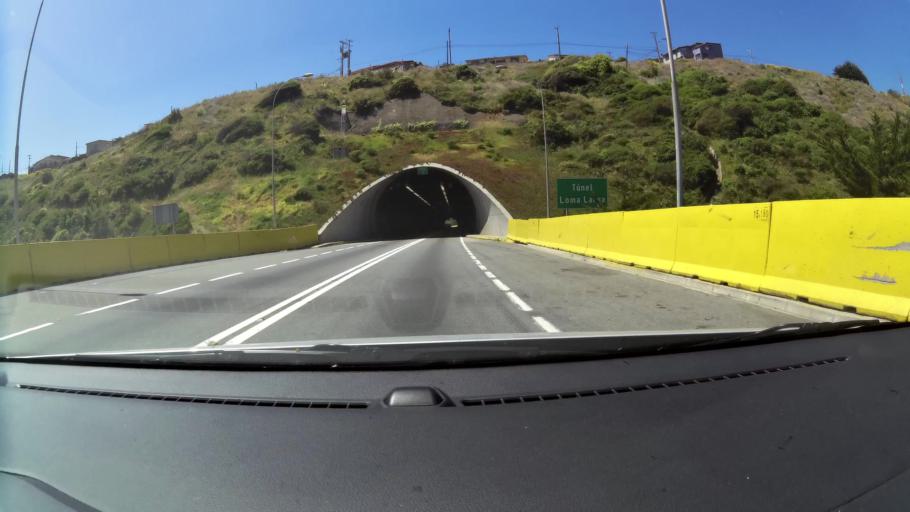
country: CL
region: Valparaiso
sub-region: Provincia de Valparaiso
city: Valparaiso
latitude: -33.0420
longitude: -71.6535
